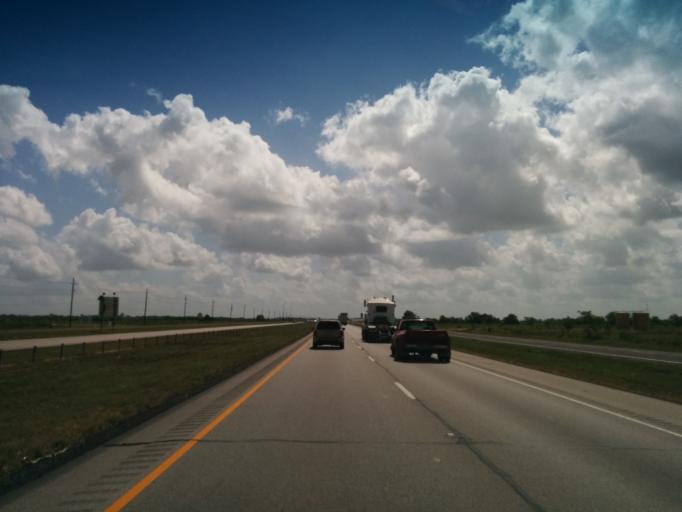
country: US
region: Texas
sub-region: Austin County
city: Sealy
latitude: 29.7615
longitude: -96.2037
